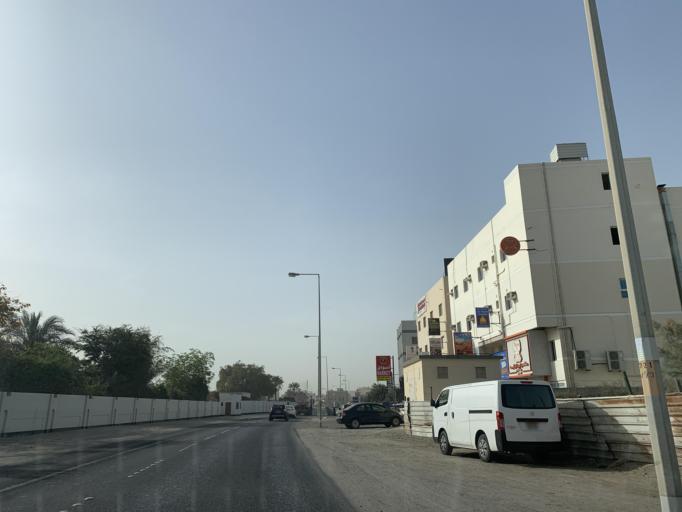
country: BH
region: Northern
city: Madinat `Isa
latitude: 26.1835
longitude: 50.5593
